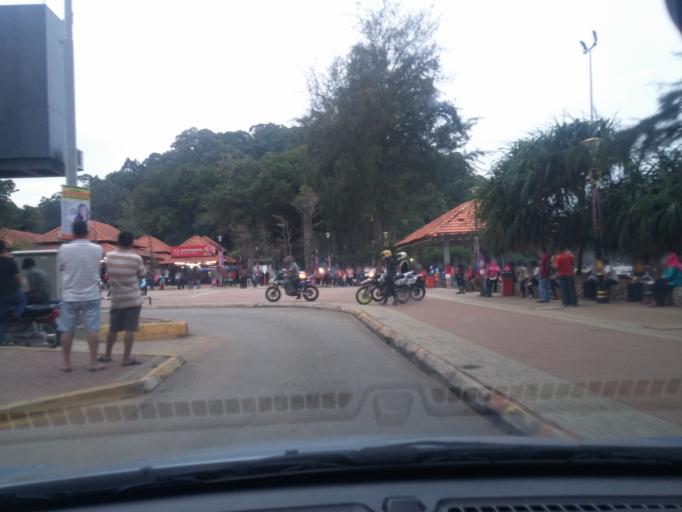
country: MY
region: Pahang
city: Kuantan
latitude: 3.8127
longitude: 103.3721
